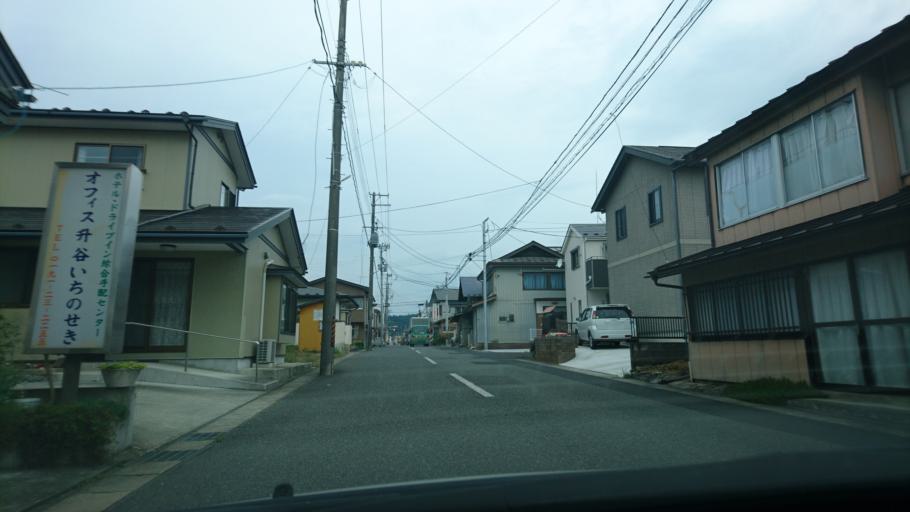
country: JP
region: Iwate
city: Ichinoseki
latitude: 38.9351
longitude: 141.1310
